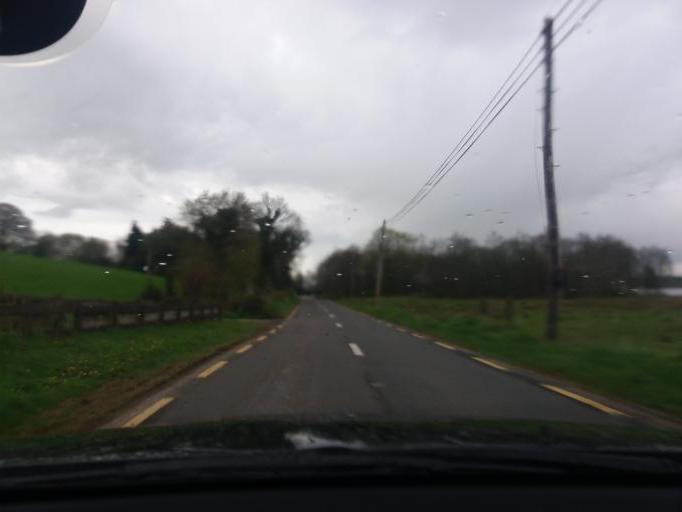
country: IE
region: Ulster
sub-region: An Cabhan
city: Ballyconnell
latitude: 54.1421
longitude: -7.7010
